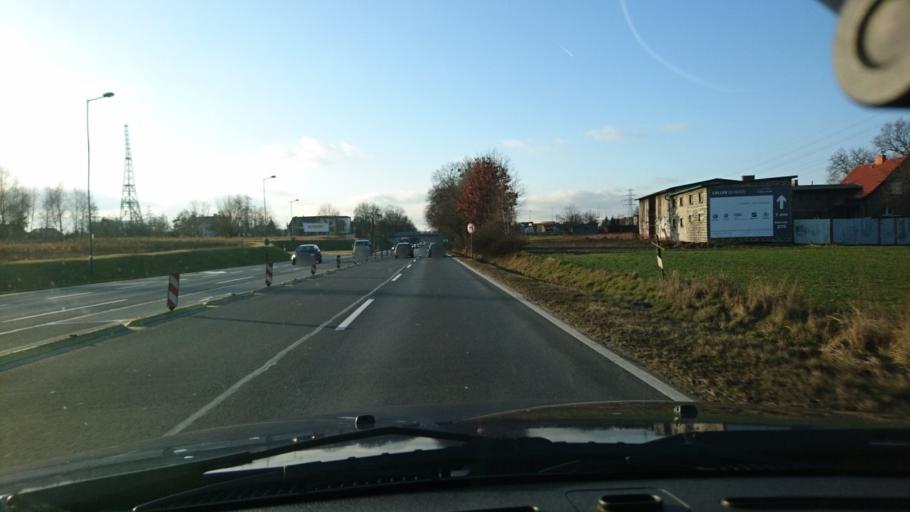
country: PL
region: Silesian Voivodeship
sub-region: Gliwice
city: Gliwice
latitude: 50.3144
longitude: 18.6972
